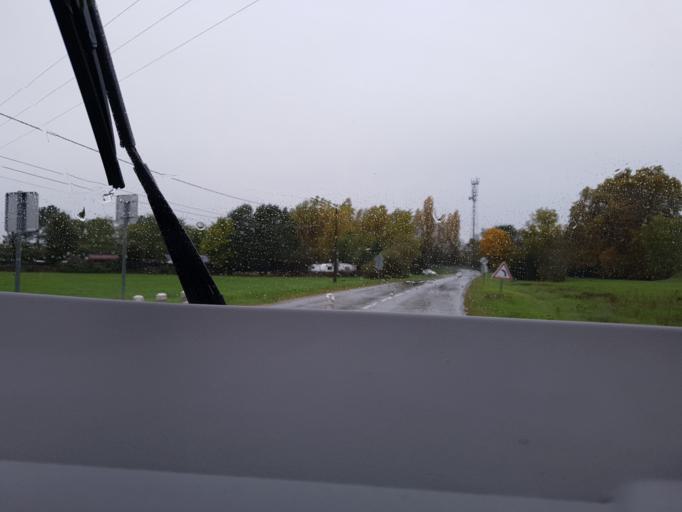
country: FR
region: Aquitaine
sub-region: Departement de la Gironde
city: Peujard
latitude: 45.0289
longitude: -0.4367
